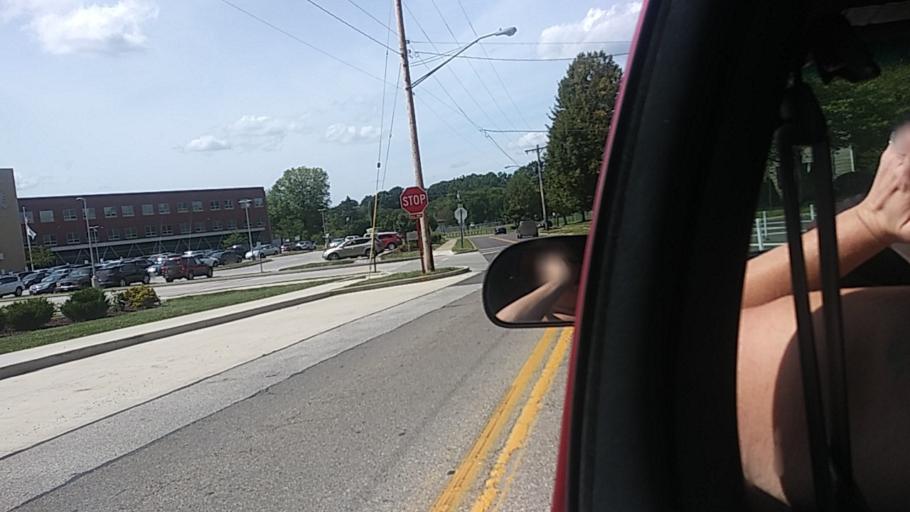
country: US
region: Ohio
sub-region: Summit County
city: Fairlawn
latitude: 41.1184
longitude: -81.5621
